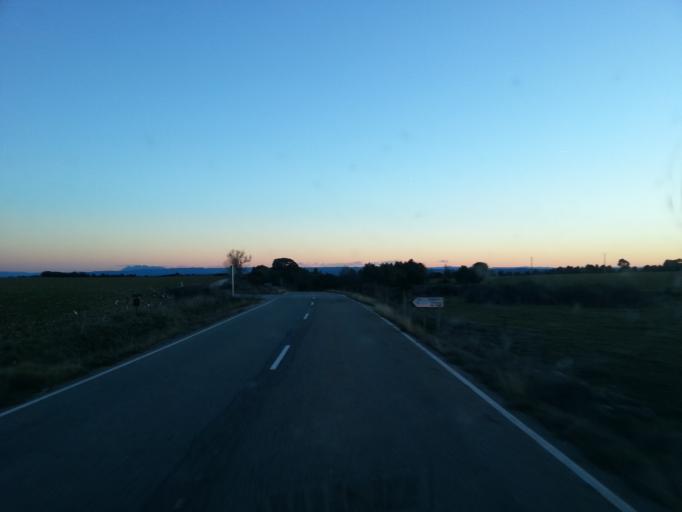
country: ES
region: Catalonia
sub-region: Provincia de Lleida
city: Solsona
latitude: 42.0657
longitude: 1.5107
